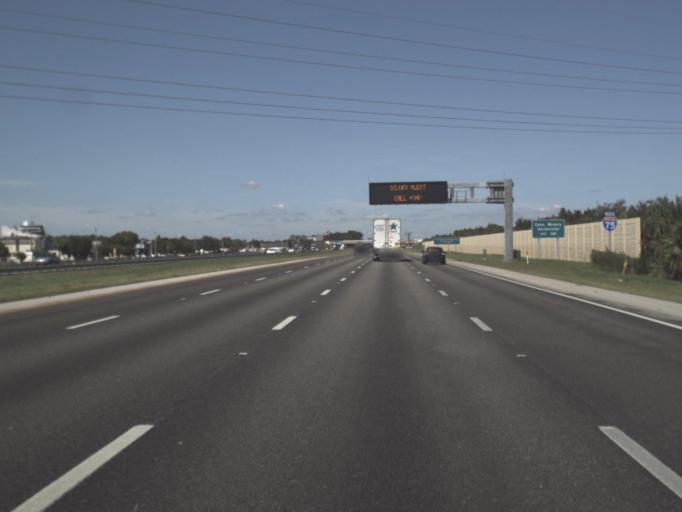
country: US
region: Florida
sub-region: Lee County
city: Tice
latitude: 26.6628
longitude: -81.7994
